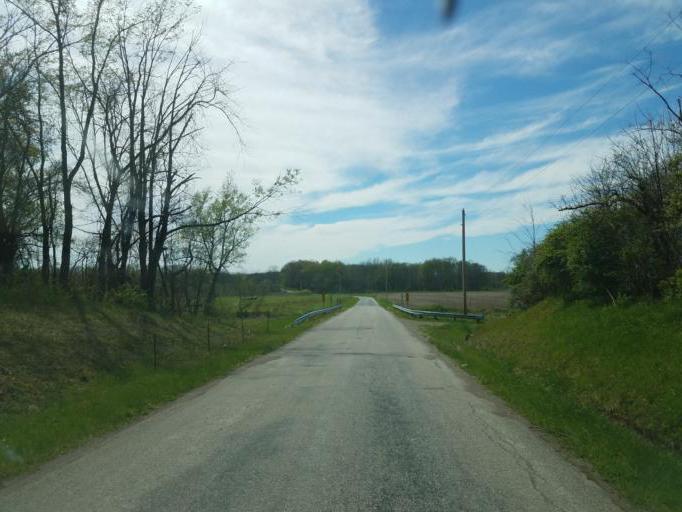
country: US
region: Ohio
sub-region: Richland County
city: Lincoln Heights
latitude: 40.8950
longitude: -82.5060
